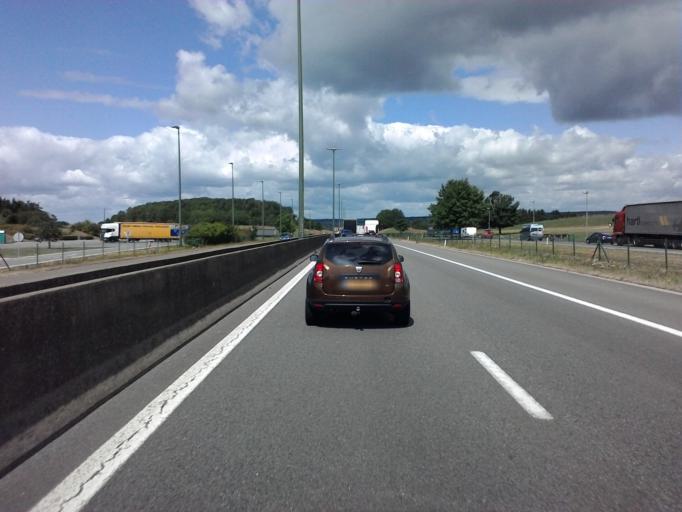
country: BE
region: Wallonia
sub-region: Province du Luxembourg
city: Habay-la-Vieille
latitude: 49.7129
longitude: 5.6078
